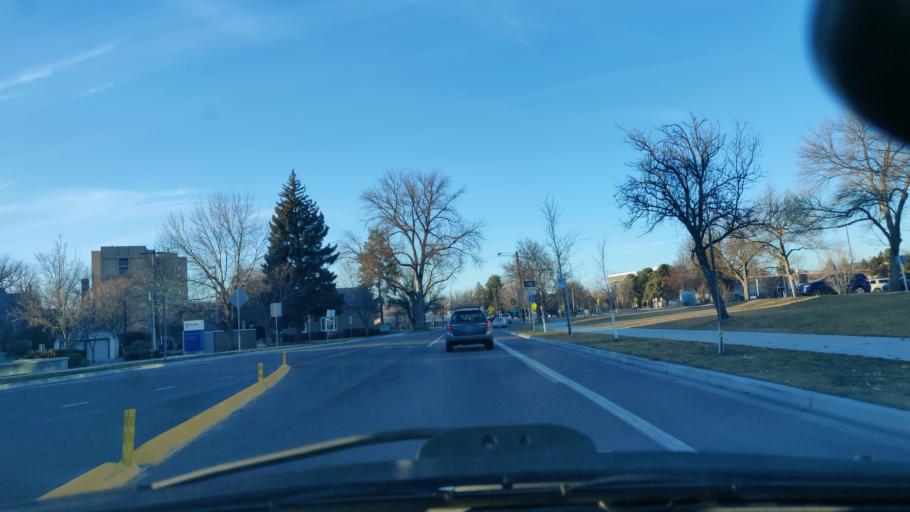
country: US
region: Idaho
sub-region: Ada County
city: Boise
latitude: 43.6151
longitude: -116.1923
